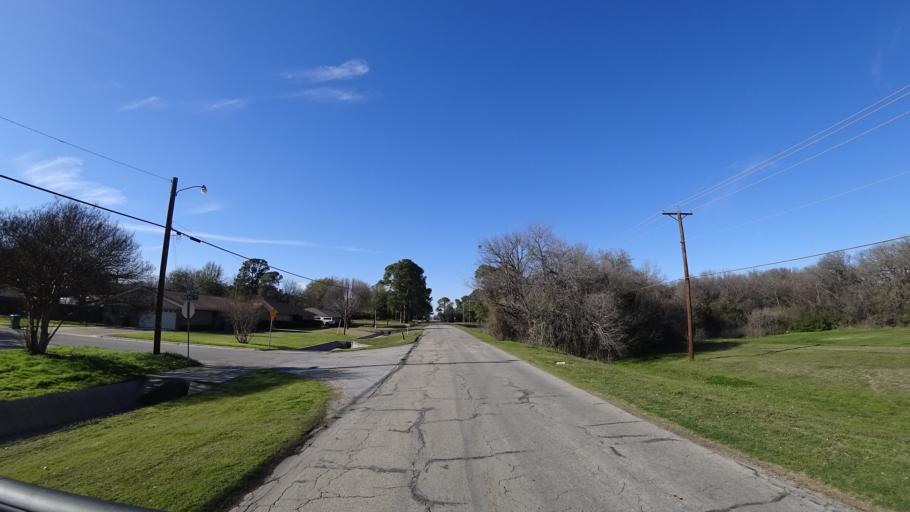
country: US
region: Texas
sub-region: Denton County
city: Lewisville
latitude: 33.0746
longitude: -97.0109
